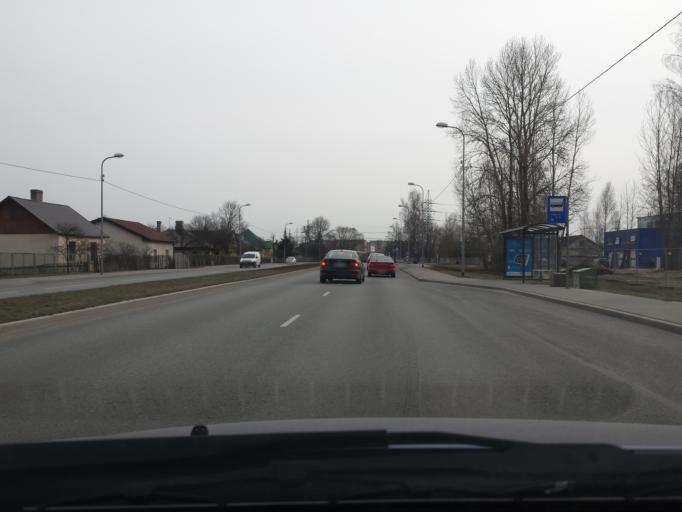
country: LV
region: Riga
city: Riga
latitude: 56.9376
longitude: 24.1821
